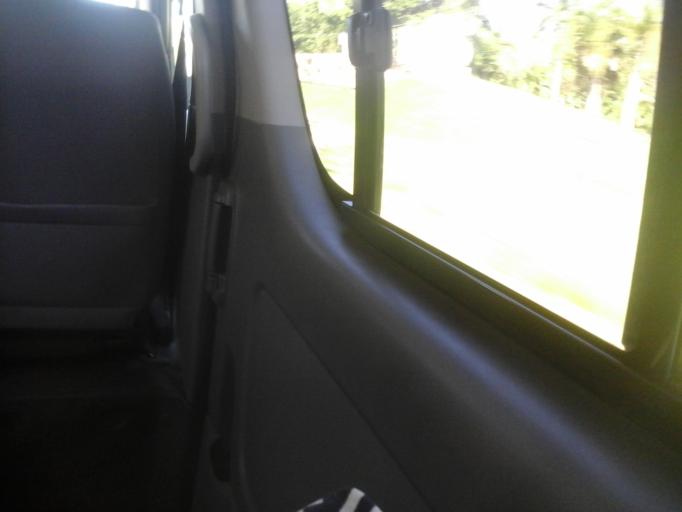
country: MX
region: Quintana Roo
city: Playa del Carmen
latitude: 20.7150
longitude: -87.0165
